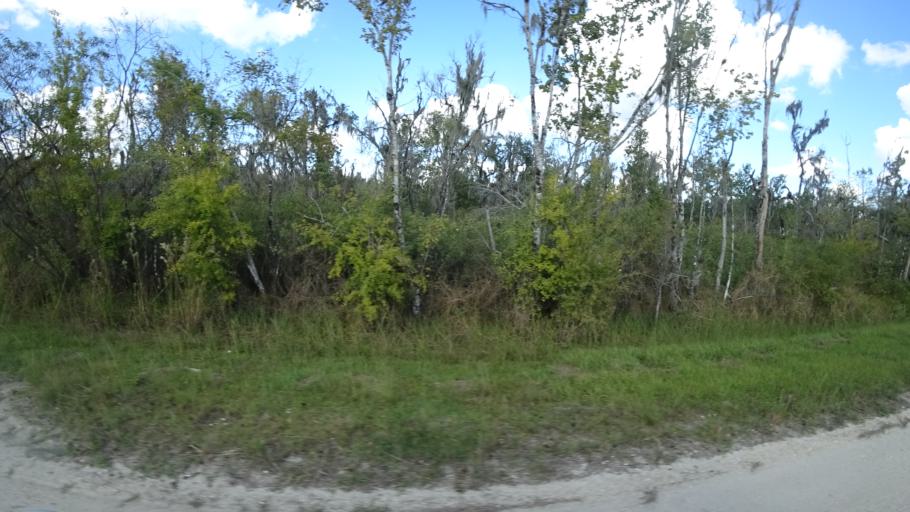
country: US
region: Florida
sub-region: Sarasota County
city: Lake Sarasota
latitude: 27.4229
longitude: -82.1400
